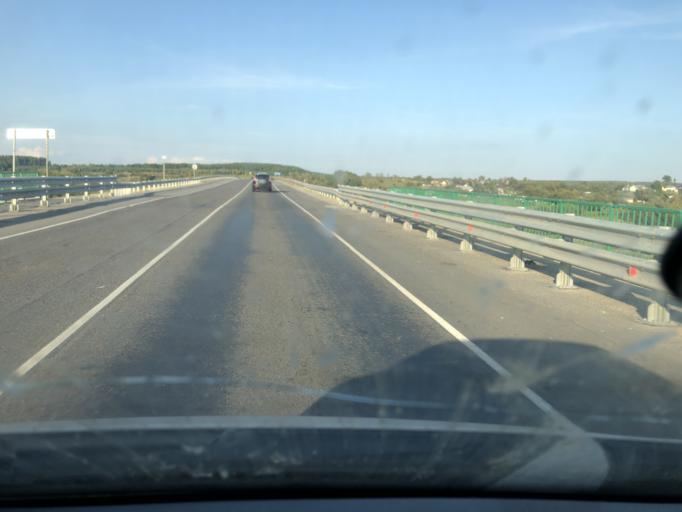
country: RU
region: Kaluga
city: Peremyshl'
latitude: 54.2905
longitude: 36.1711
